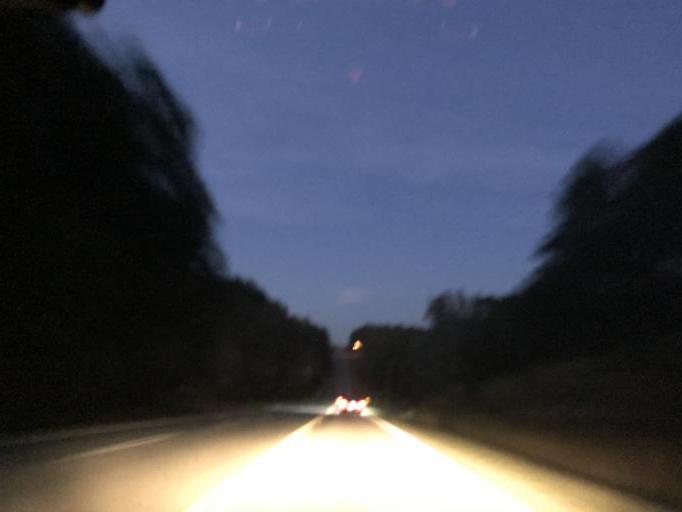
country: US
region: Georgia
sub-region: Jones County
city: Gray
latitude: 32.9069
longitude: -83.5217
